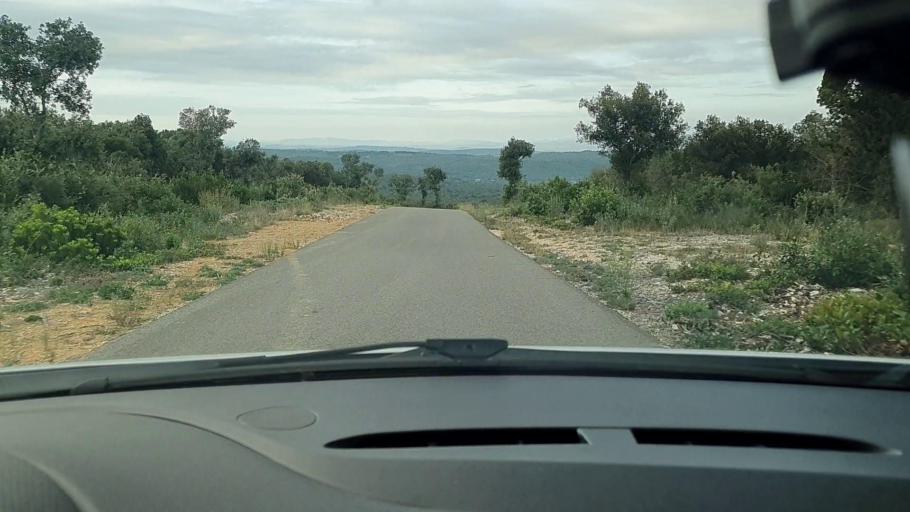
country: FR
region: Languedoc-Roussillon
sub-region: Departement du Gard
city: Mons
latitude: 44.1415
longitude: 4.2627
